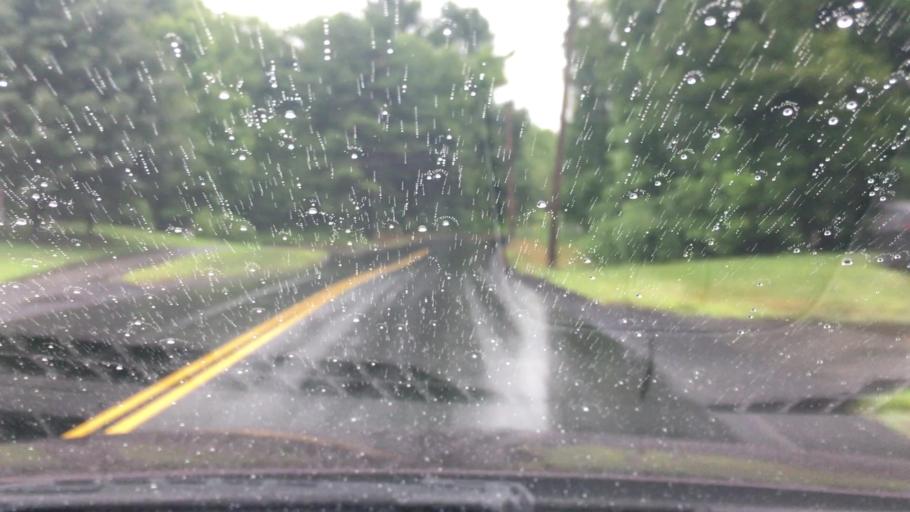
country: US
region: Connecticut
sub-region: Tolland County
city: Stafford Springs
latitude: 41.9760
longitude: -72.3280
